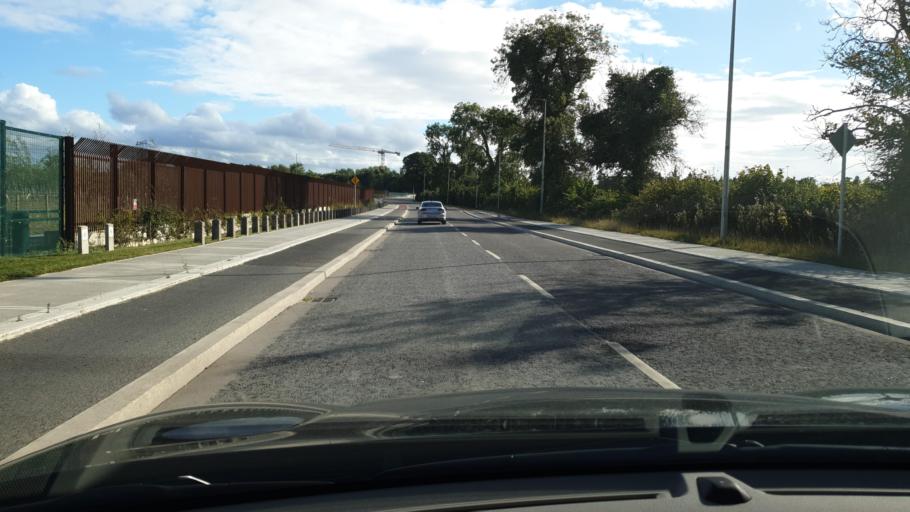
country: IE
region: Leinster
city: Hartstown
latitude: 53.4169
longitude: -6.4399
